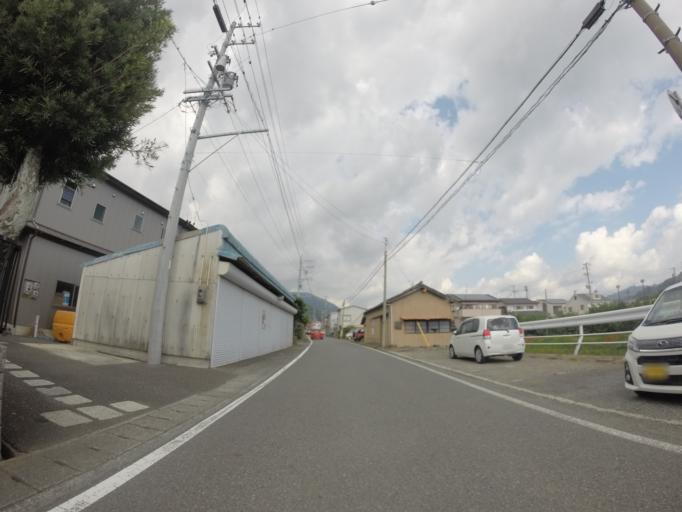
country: JP
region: Shizuoka
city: Shizuoka-shi
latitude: 35.0507
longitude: 138.4776
